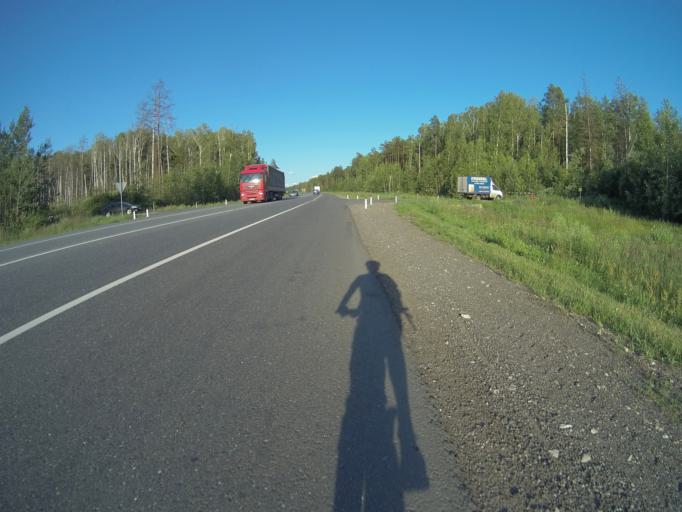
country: RU
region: Vladimir
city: Raduzhnyy
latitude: 56.0653
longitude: 40.3176
